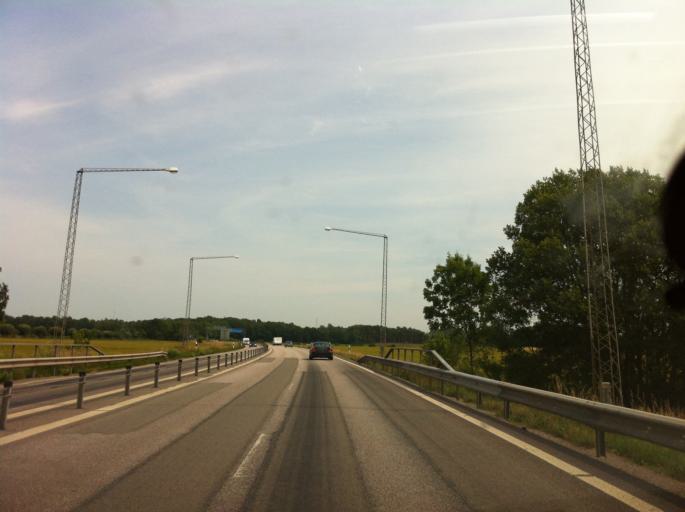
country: SE
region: Kalmar
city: Faerjestaden
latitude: 56.6667
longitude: 16.4926
